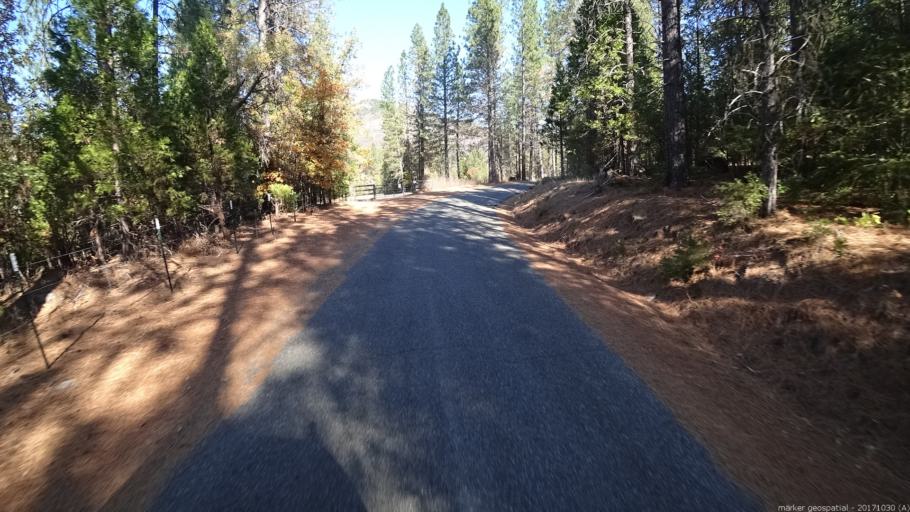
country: US
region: California
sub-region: Shasta County
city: Shingletown
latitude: 40.5644
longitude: -121.8936
